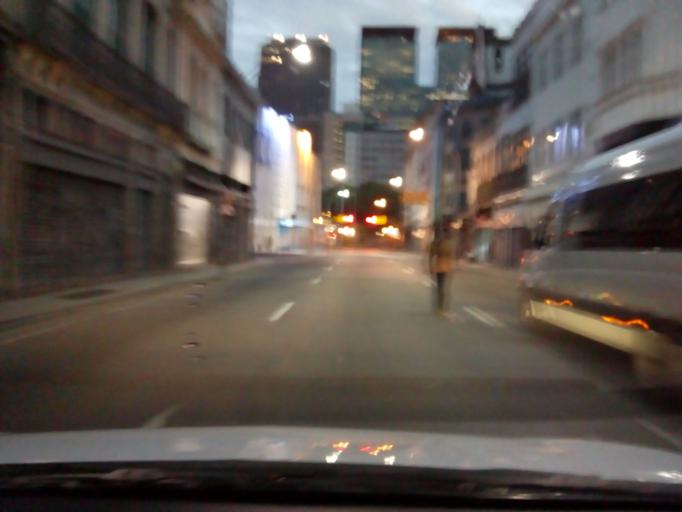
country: BR
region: Rio de Janeiro
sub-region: Rio De Janeiro
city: Rio de Janeiro
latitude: -22.9053
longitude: -43.1829
